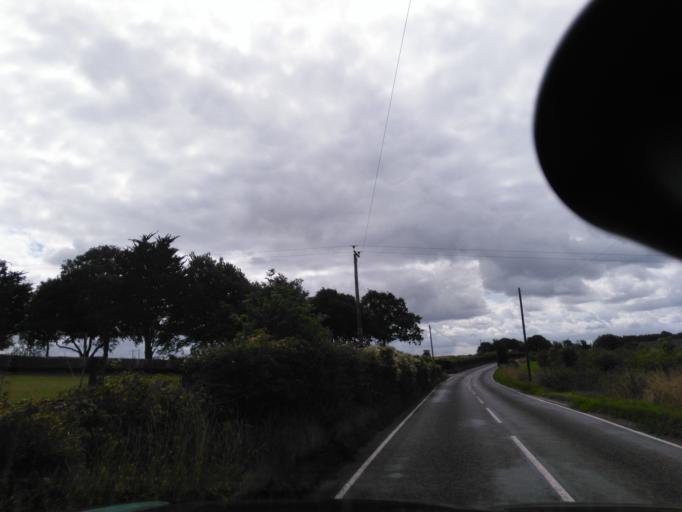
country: GB
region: England
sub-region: Dorset
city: Blandford Forum
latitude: 50.9022
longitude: -2.1558
